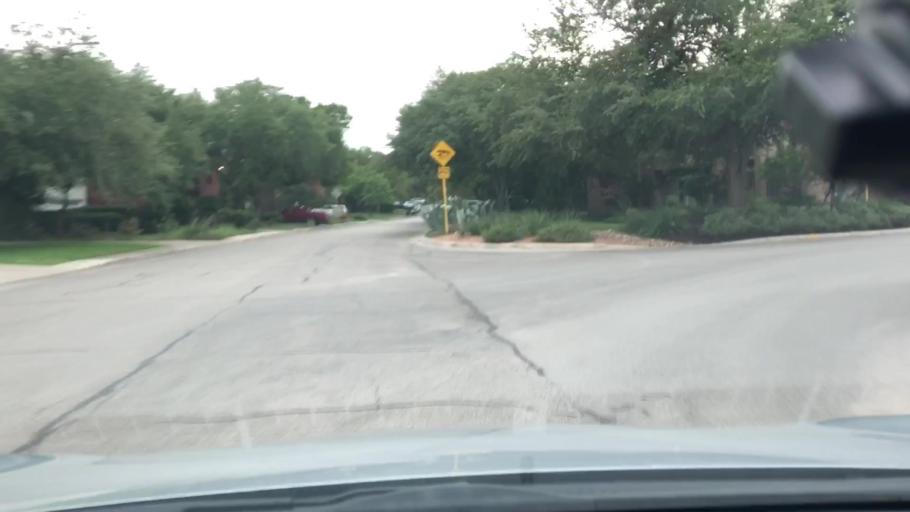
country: US
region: Texas
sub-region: Bexar County
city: Leon Valley
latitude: 29.4992
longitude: -98.6653
